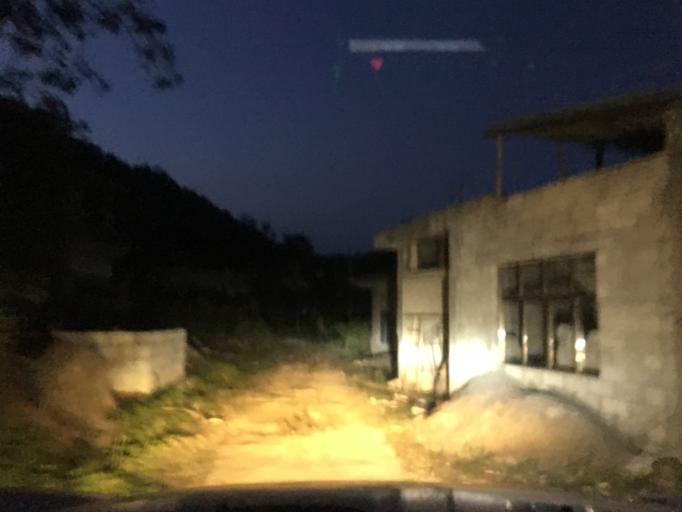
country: CN
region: Guangxi Zhuangzu Zizhiqu
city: Xinzhou
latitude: 25.3612
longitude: 105.7342
